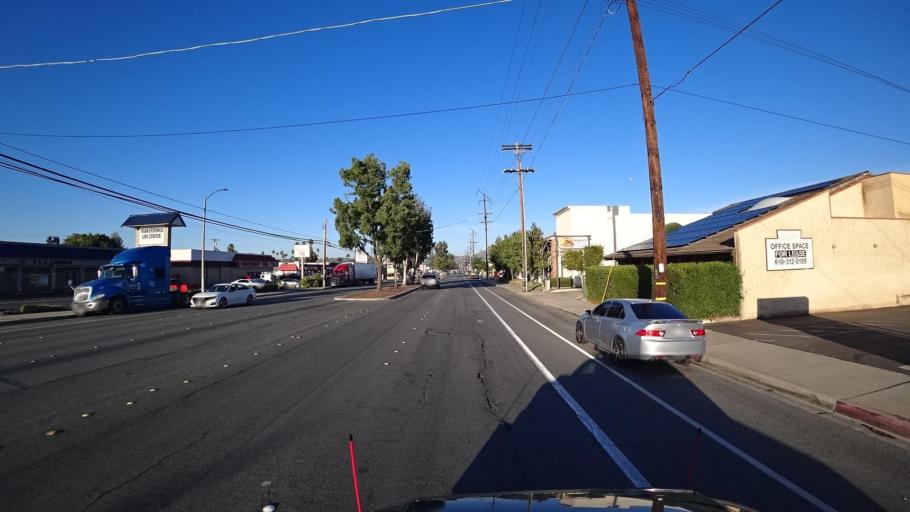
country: US
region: California
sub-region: San Diego County
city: Bostonia
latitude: 32.8078
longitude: -116.9470
